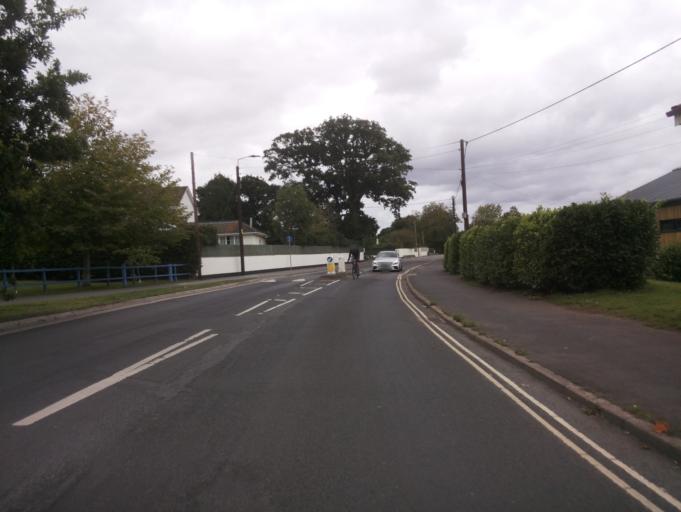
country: GB
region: England
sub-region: Devon
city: Starcross
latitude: 50.6014
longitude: -3.4483
